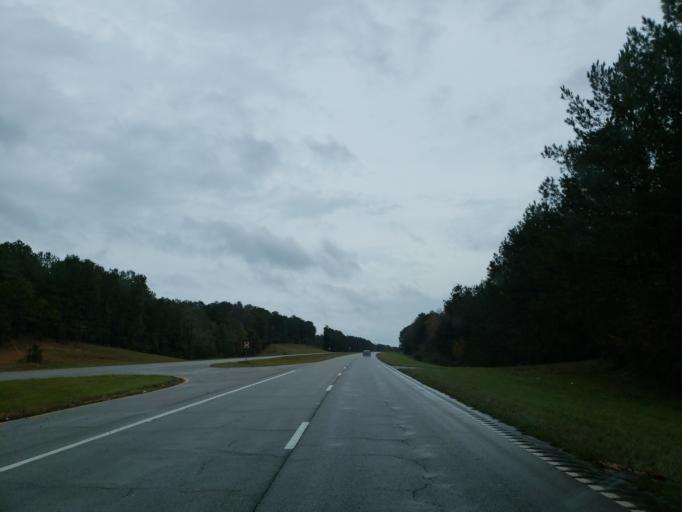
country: US
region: Mississippi
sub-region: Jones County
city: Laurel
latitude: 31.7059
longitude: -89.0677
